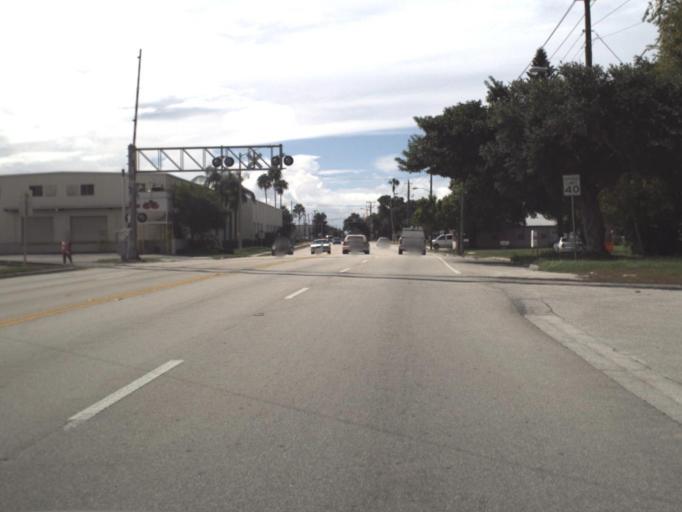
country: US
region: Florida
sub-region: Manatee County
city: Palmetto
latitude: 27.5212
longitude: -82.5661
